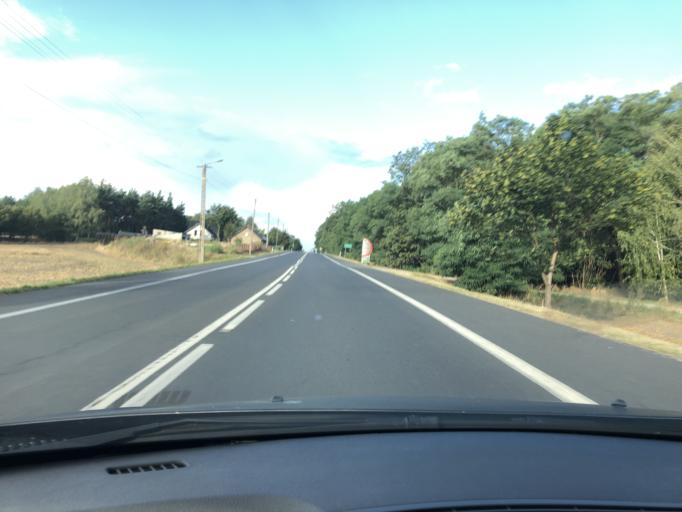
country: PL
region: Lodz Voivodeship
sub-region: Powiat wieruszowski
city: Galewice
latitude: 51.3042
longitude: 18.2326
